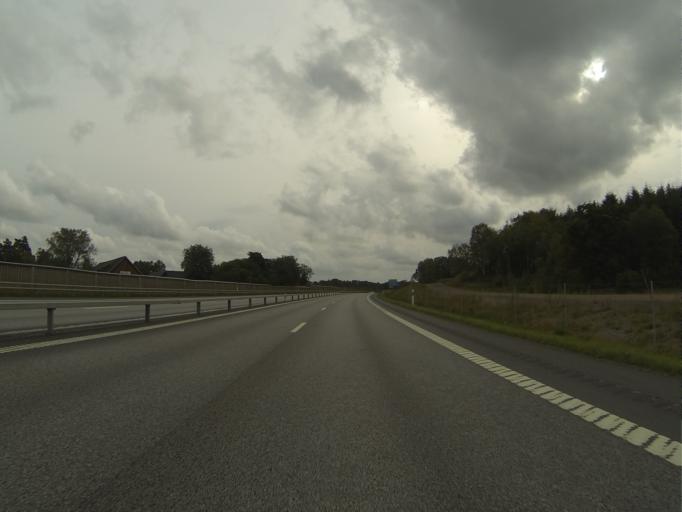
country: SE
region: Skane
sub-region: Horby Kommun
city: Hoerby
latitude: 55.8764
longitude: 13.7103
